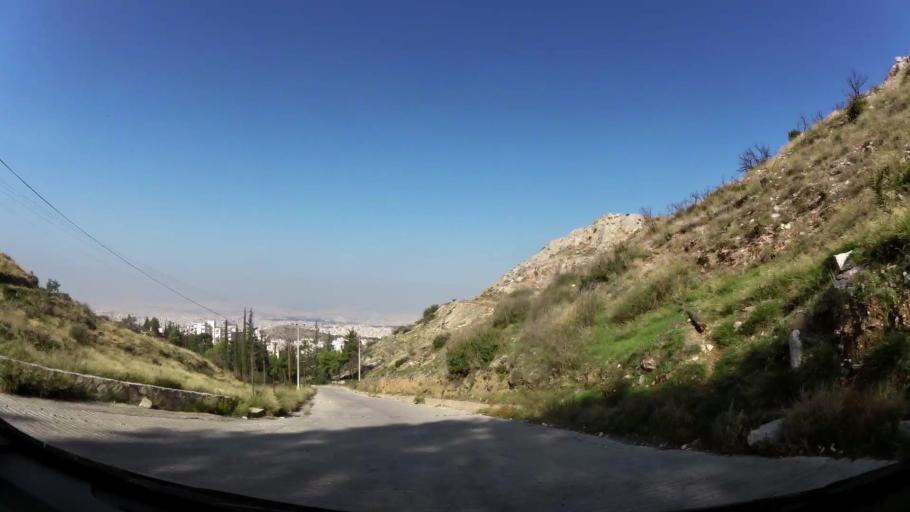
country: GR
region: Attica
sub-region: Nomarchia Athinas
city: Ilioupoli
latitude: 37.9424
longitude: 23.7776
